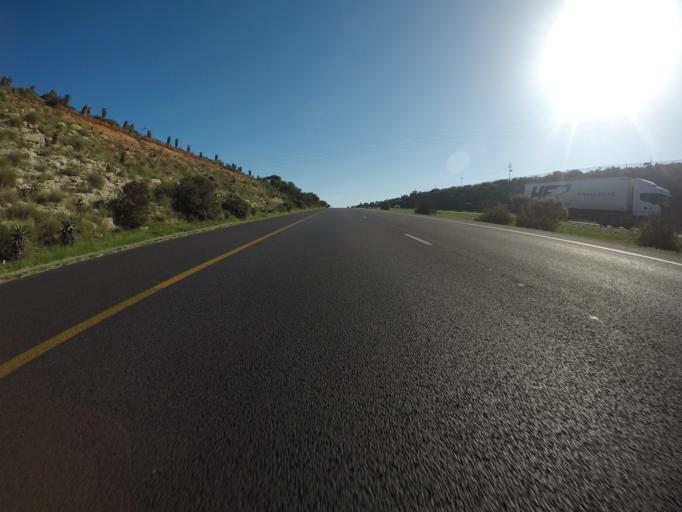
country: ZA
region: Western Cape
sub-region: Eden District Municipality
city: Mossel Bay
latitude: -34.1624
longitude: 22.0935
